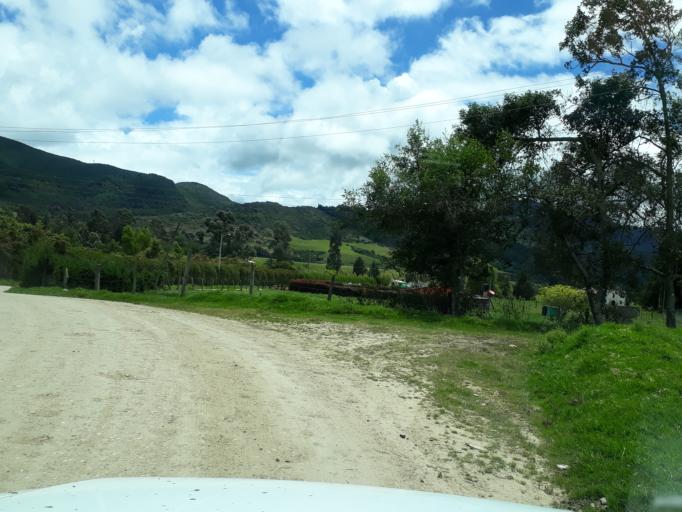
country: CO
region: Cundinamarca
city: Guasca
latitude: 4.8465
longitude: -73.9029
